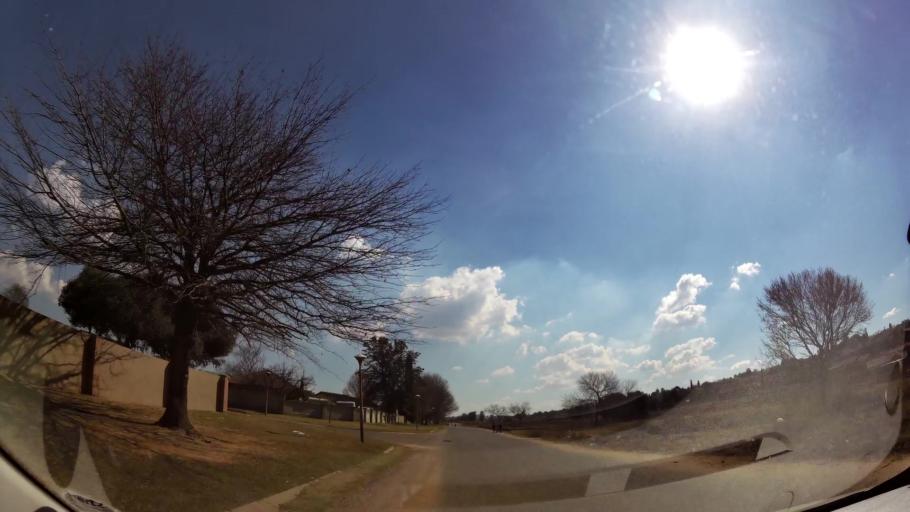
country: ZA
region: Mpumalanga
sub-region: Nkangala District Municipality
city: Witbank
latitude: -25.9381
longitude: 29.2490
